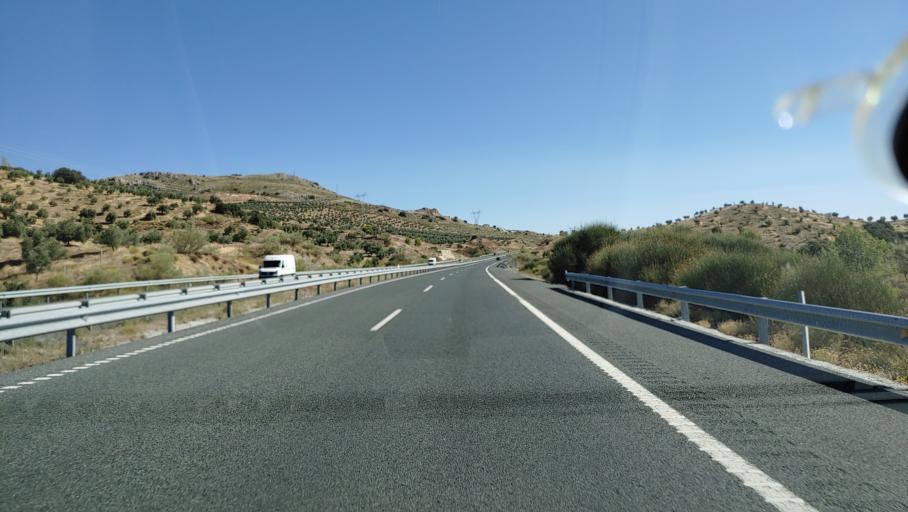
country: ES
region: Andalusia
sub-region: Provincia de Granada
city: Diezma
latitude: 37.3099
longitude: -3.3613
